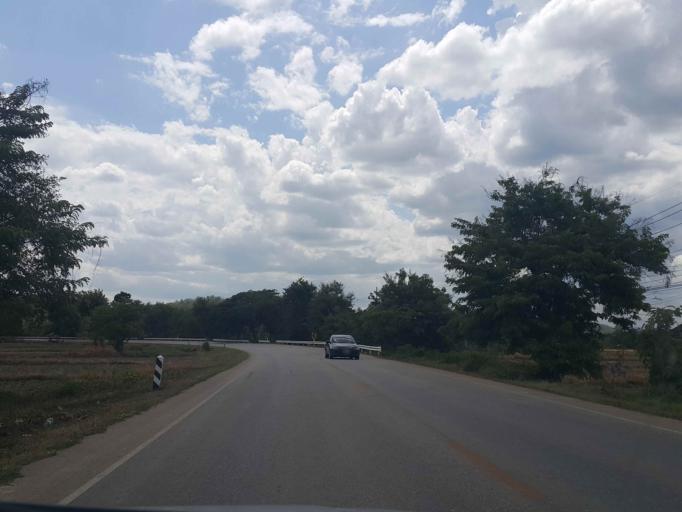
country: TH
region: Sukhothai
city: Thung Saliam
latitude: 17.3433
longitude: 99.5993
